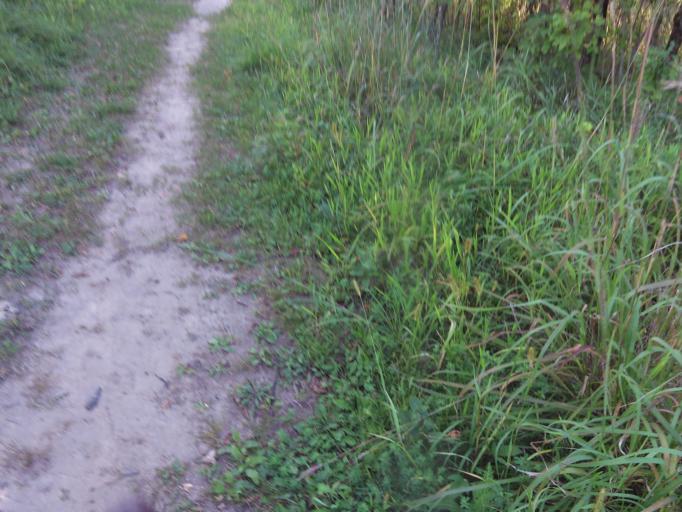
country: US
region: Minnesota
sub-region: Washington County
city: Afton
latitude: 44.8506
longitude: -92.7747
